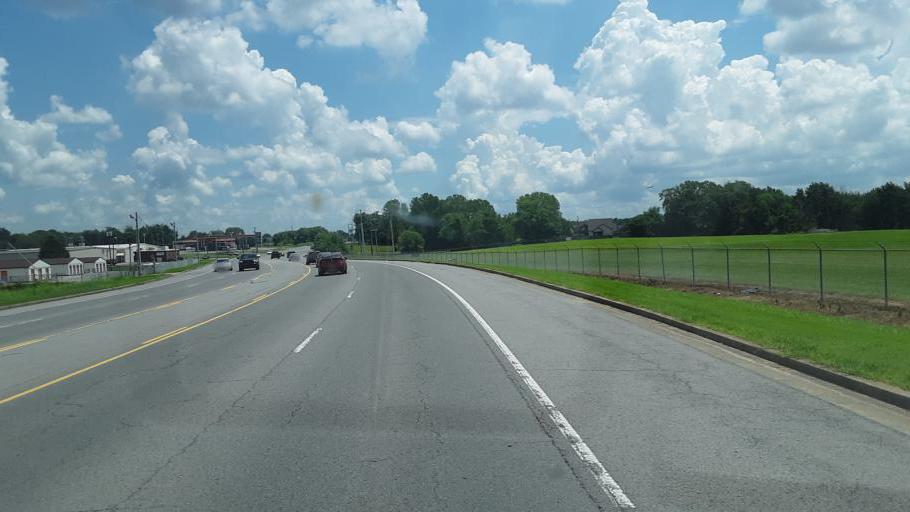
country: US
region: Kentucky
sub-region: Christian County
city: Oak Grove
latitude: 36.6325
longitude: -87.4190
